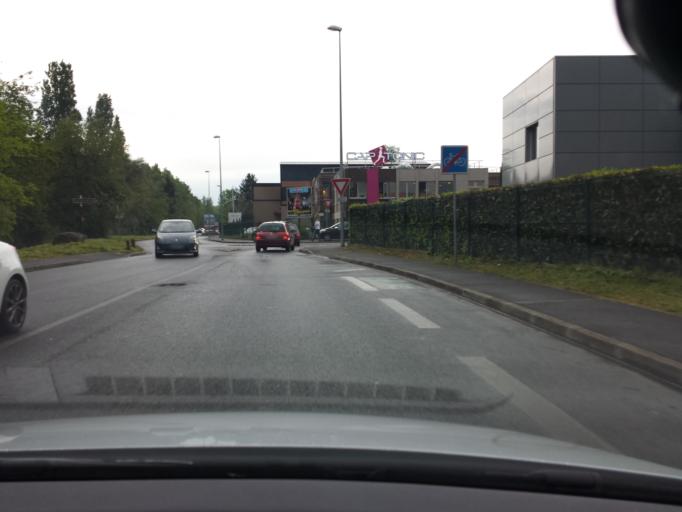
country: FR
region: Ile-de-France
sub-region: Departement de l'Essonne
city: Verrieres-le-Buisson
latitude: 48.7450
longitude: 2.2825
